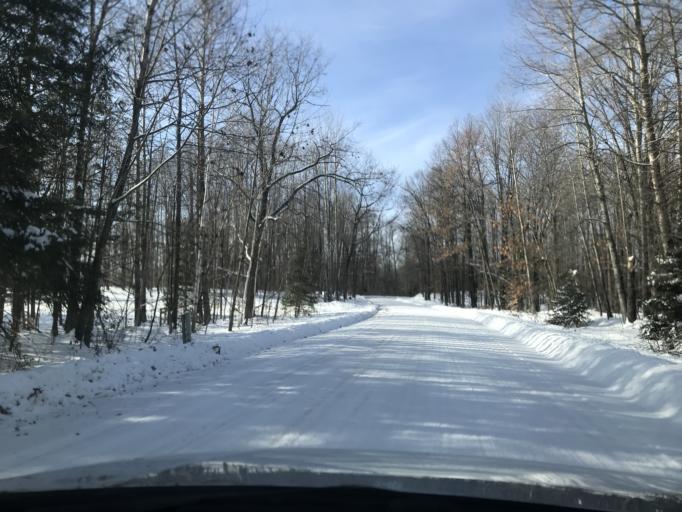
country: US
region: Wisconsin
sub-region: Oconto County
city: Gillett
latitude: 45.1461
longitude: -88.2326
